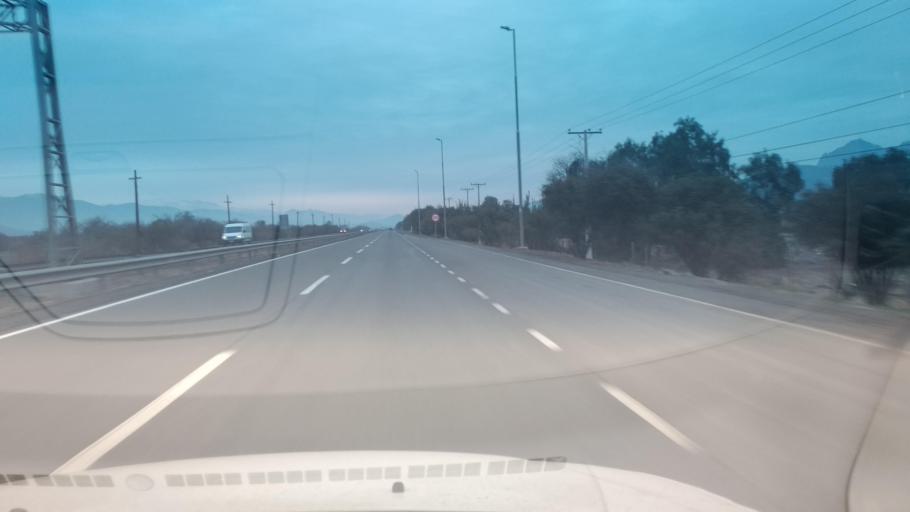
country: CL
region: Santiago Metropolitan
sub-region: Provincia de Chacabuco
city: Chicureo Abajo
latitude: -33.0980
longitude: -70.6921
